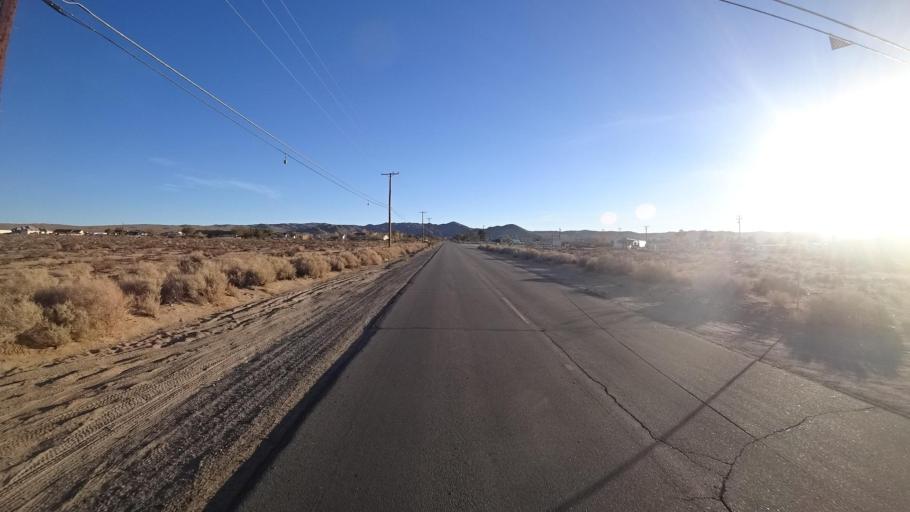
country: US
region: California
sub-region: Kern County
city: Ridgecrest
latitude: 35.6024
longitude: -117.6526
